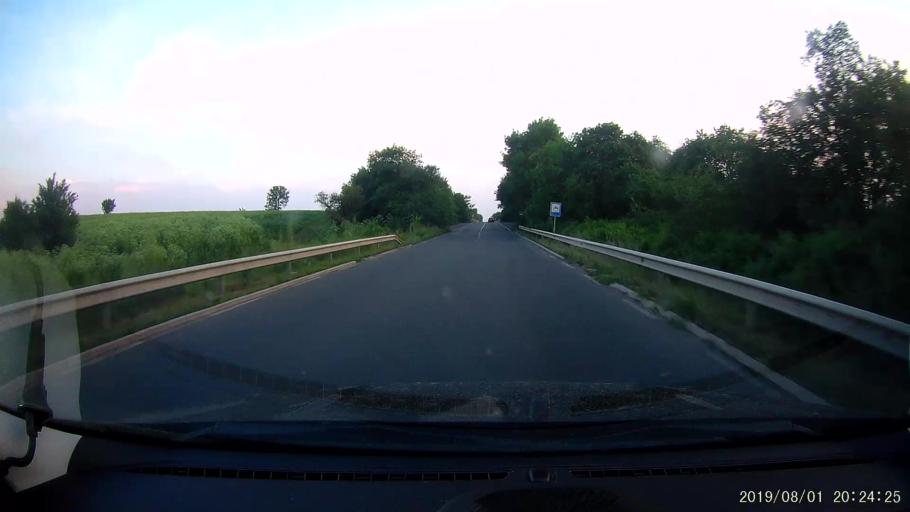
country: BG
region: Yambol
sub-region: Obshtina Elkhovo
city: Elkhovo
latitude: 42.2318
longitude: 26.5936
